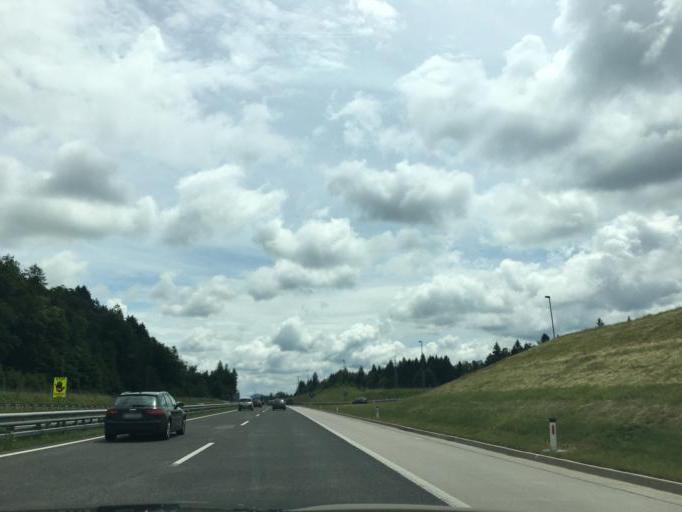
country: SI
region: Radovljica
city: Radovljica
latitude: 46.3383
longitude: 14.1923
